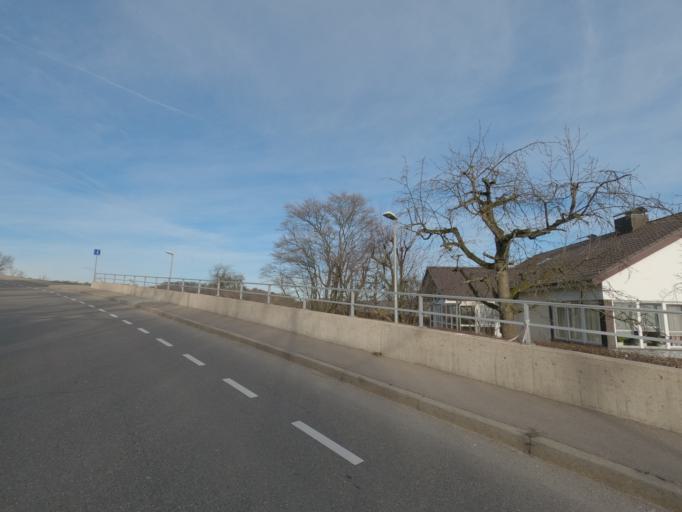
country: DE
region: Baden-Wuerttemberg
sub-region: Regierungsbezirk Stuttgart
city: Uhingen
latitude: 48.7019
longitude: 9.5800
